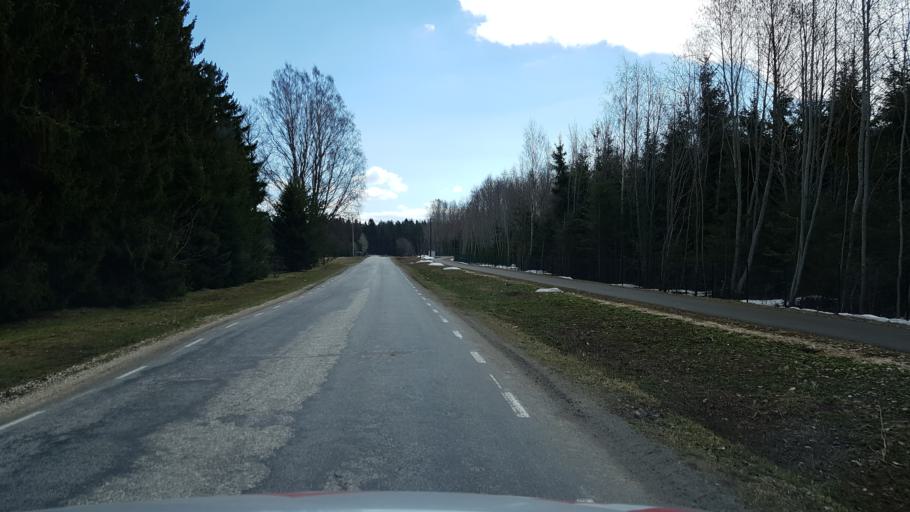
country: EE
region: Laeaene-Virumaa
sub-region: Haljala vald
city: Haljala
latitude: 59.3910
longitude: 26.2916
